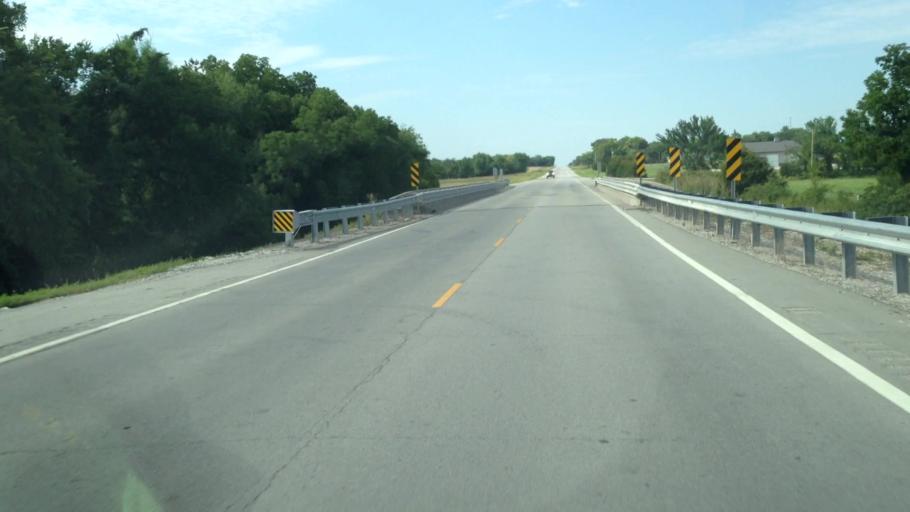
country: US
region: Kansas
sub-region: Labette County
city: Parsons
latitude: 37.2942
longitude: -95.2675
